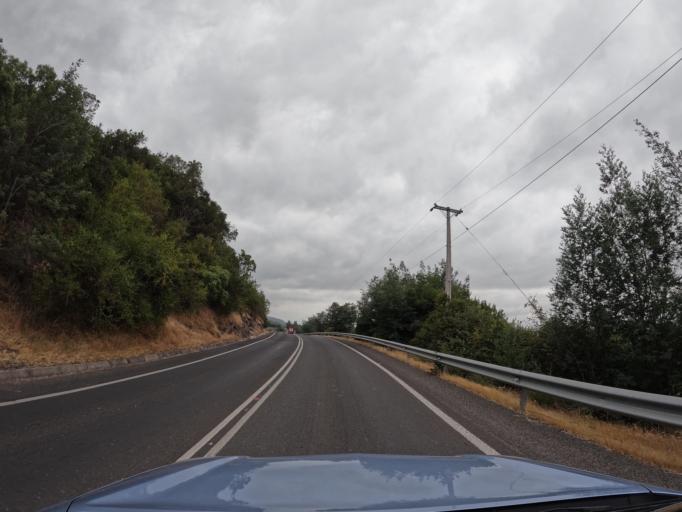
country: CL
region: O'Higgins
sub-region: Provincia de Colchagua
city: Chimbarongo
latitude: -34.7261
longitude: -71.0936
